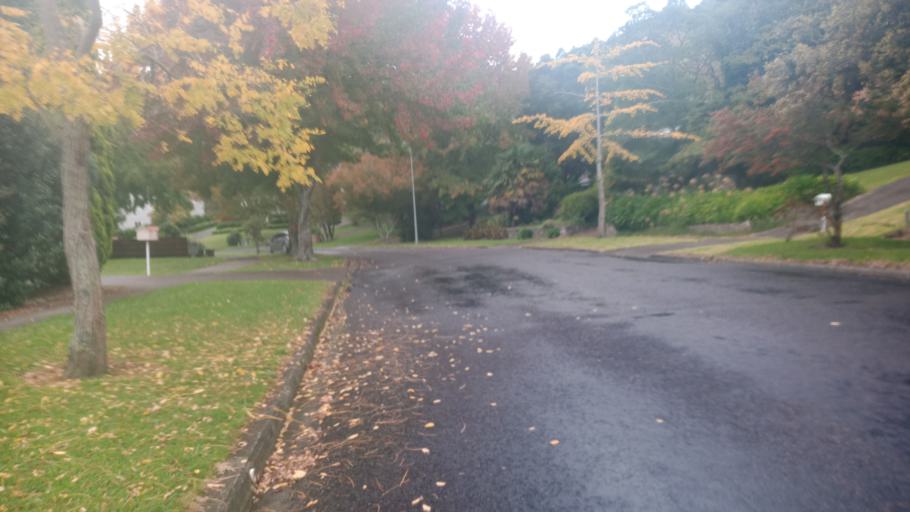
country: NZ
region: Gisborne
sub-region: Gisborne District
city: Gisborne
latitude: -38.6587
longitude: 178.0405
